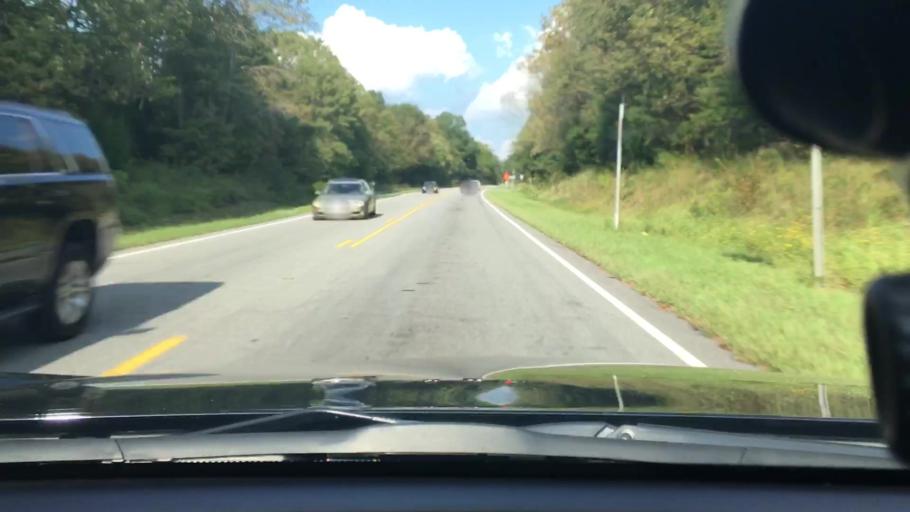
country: US
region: North Carolina
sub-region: Randolph County
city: Asheboro
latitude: 35.6710
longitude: -79.8742
